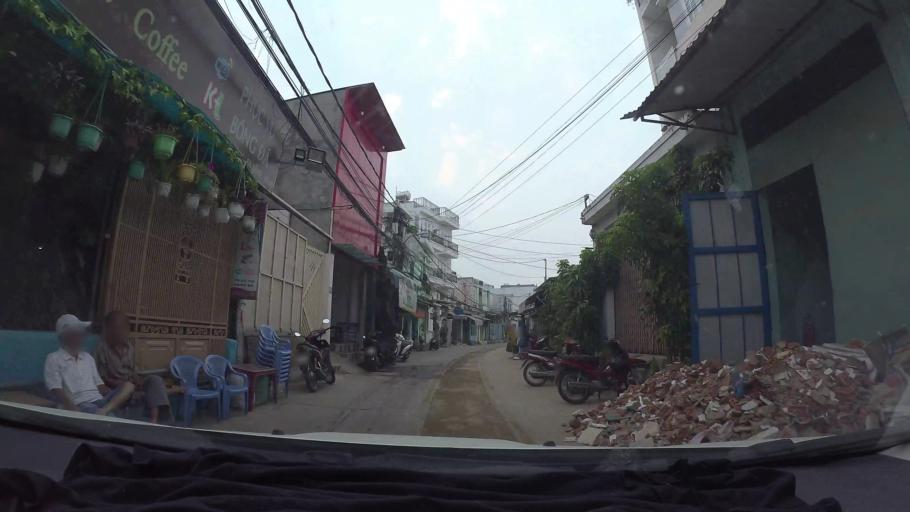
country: VN
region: Da Nang
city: Thanh Khe
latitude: 16.0678
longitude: 108.2035
